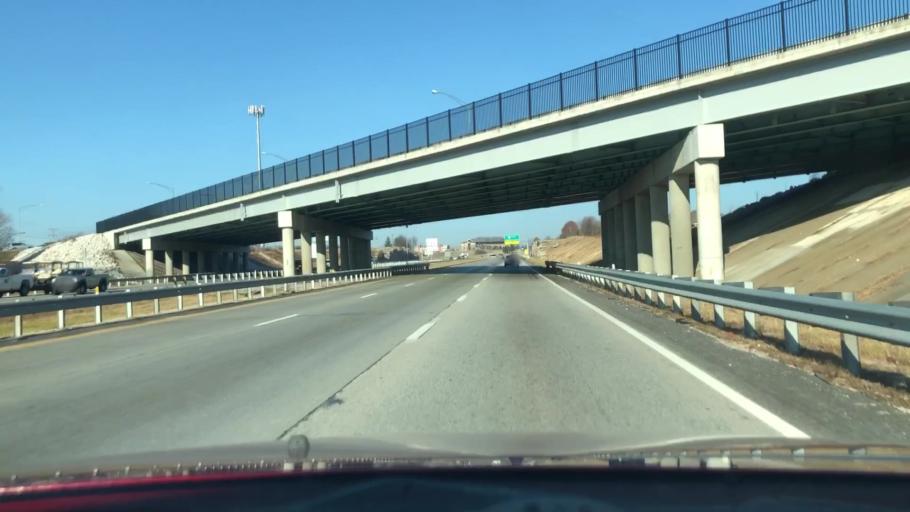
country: US
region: Missouri
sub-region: Greene County
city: Battlefield
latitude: 37.1380
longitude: -93.3100
